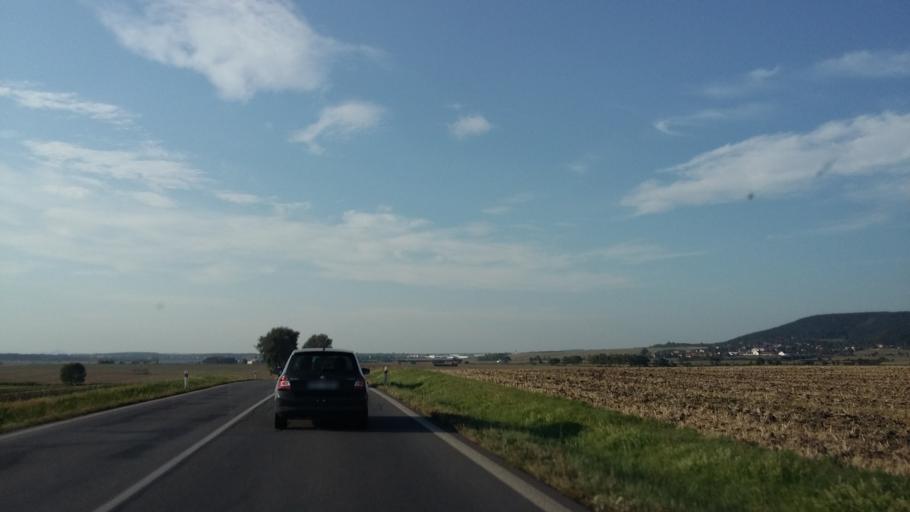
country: CZ
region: Central Bohemia
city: Lustenice
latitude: 50.3584
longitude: 14.9100
